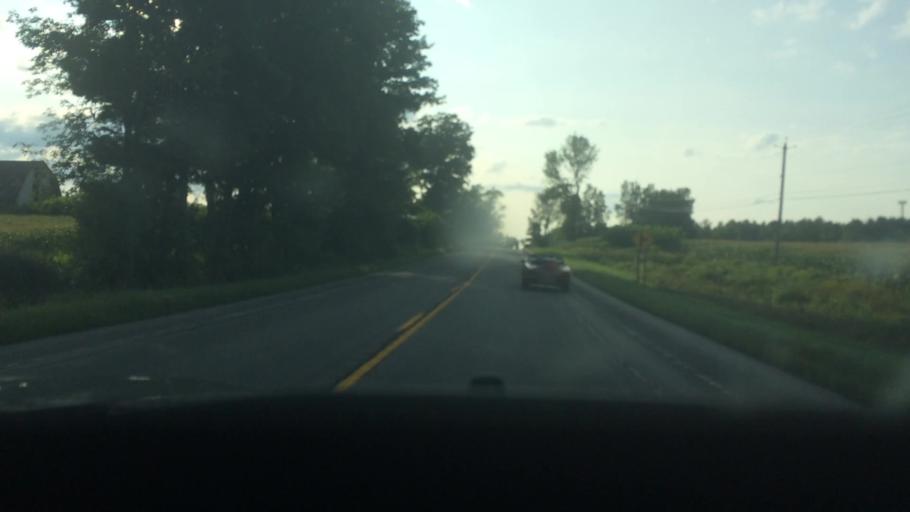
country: US
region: New York
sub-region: St. Lawrence County
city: Canton
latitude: 44.6479
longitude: -75.2880
